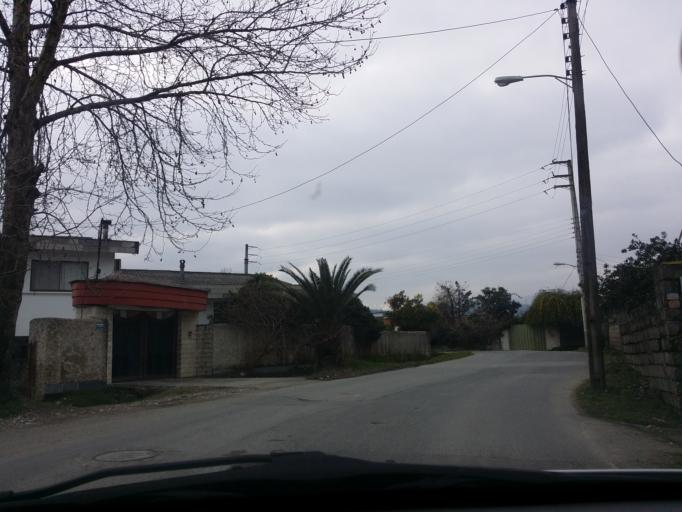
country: IR
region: Mazandaran
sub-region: Nowshahr
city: Nowshahr
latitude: 36.6468
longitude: 51.4833
